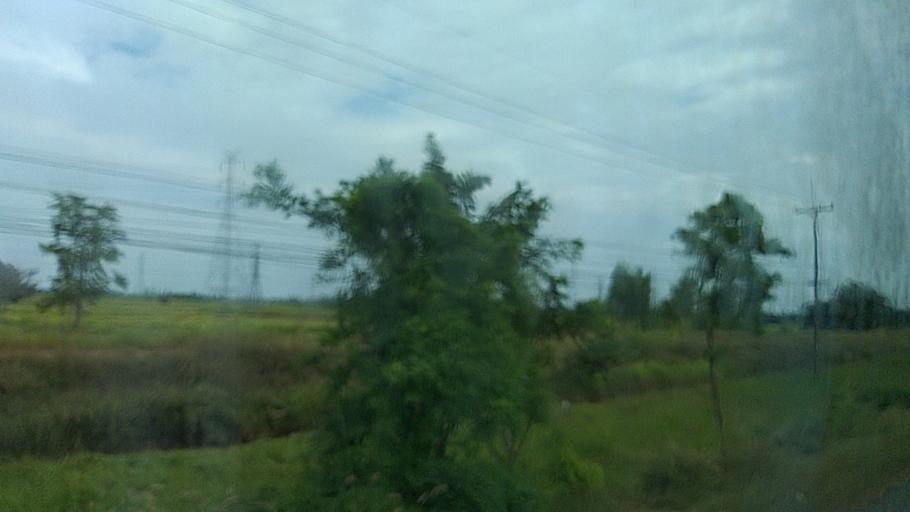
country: TH
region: Roi Et
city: Si Somdet
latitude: 16.1253
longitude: 103.4755
